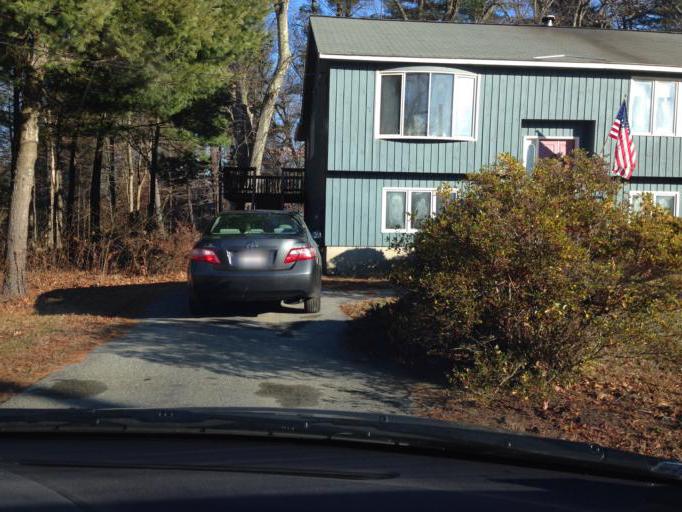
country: US
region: Massachusetts
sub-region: Middlesex County
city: Bedford
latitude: 42.5255
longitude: -71.2845
